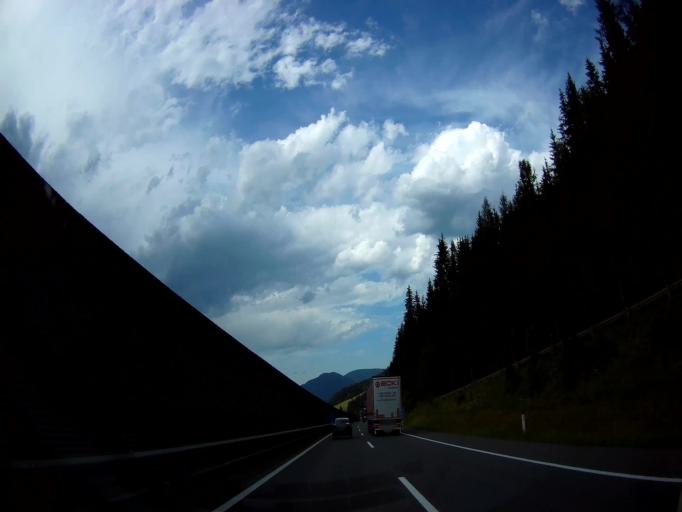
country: AT
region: Salzburg
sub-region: Politischer Bezirk Sankt Johann im Pongau
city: Flachau
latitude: 47.3528
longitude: 13.3984
